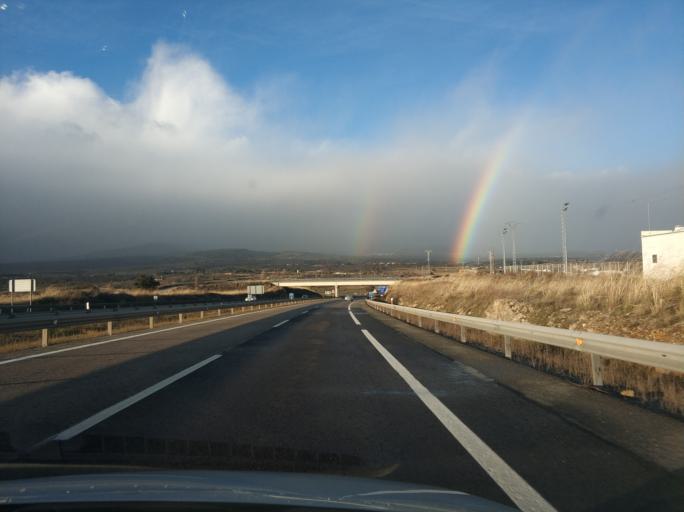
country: ES
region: Madrid
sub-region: Provincia de Madrid
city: Buitrago del Lozoya
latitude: 40.9897
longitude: -3.6419
